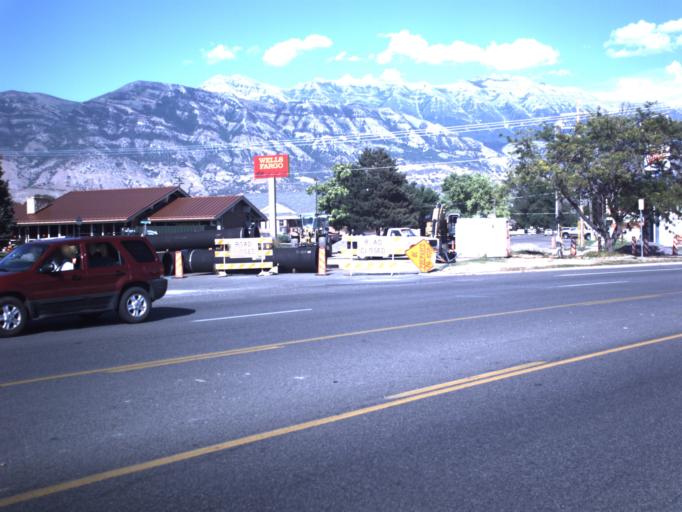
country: US
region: Utah
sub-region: Utah County
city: American Fork
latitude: 40.3766
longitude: -111.7939
